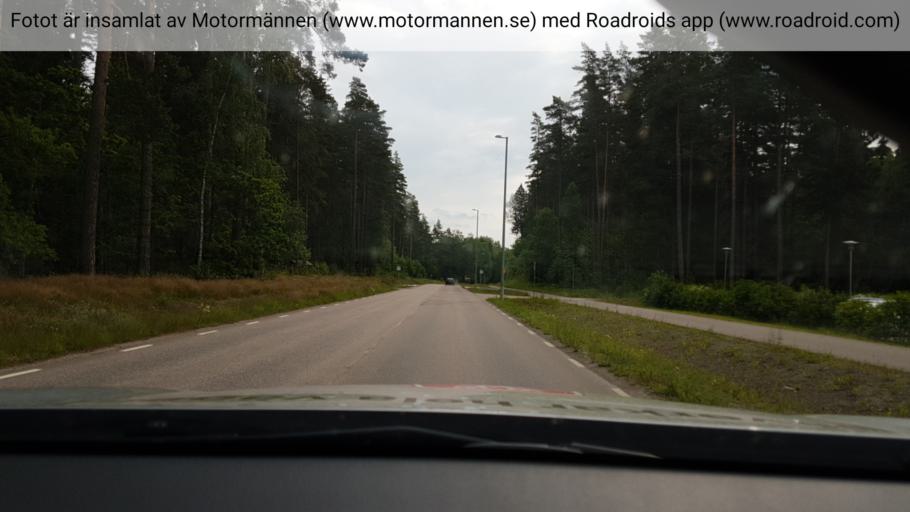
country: SE
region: Vaestra Goetaland
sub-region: Skovde Kommun
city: Skultorp
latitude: 58.3415
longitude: 13.8512
